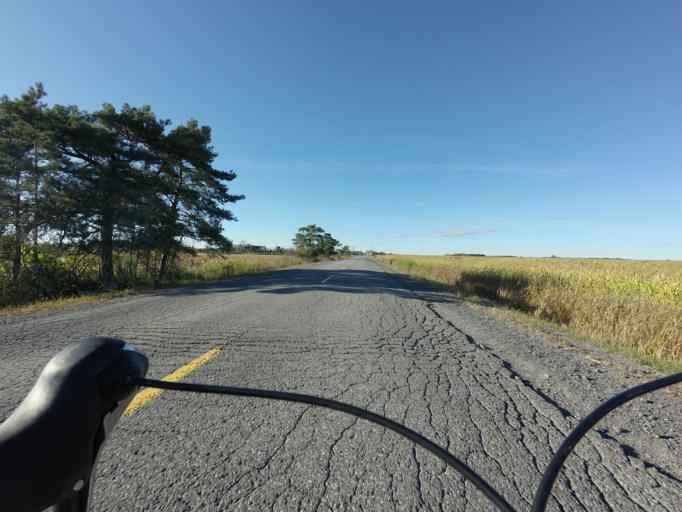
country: CA
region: Ontario
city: Bells Corners
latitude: 45.2018
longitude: -75.7913
